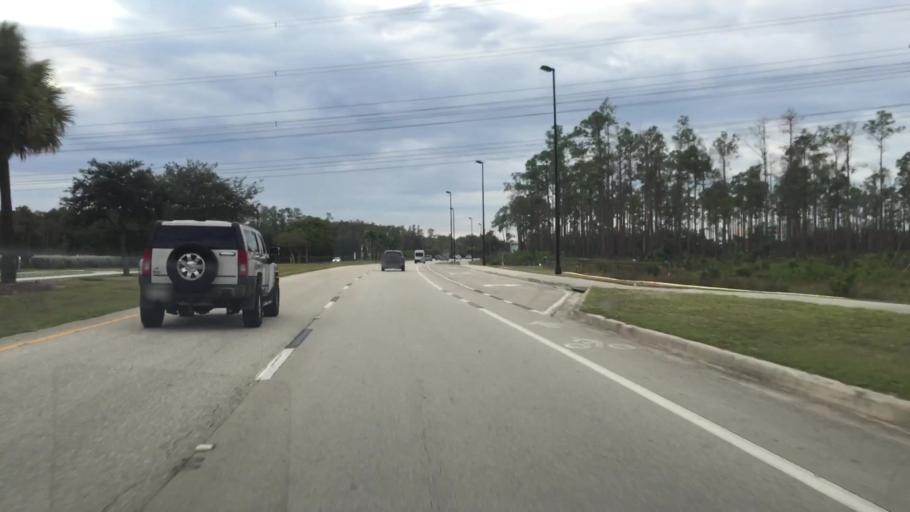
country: US
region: Florida
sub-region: Lee County
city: Three Oaks
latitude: 26.5005
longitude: -81.7846
